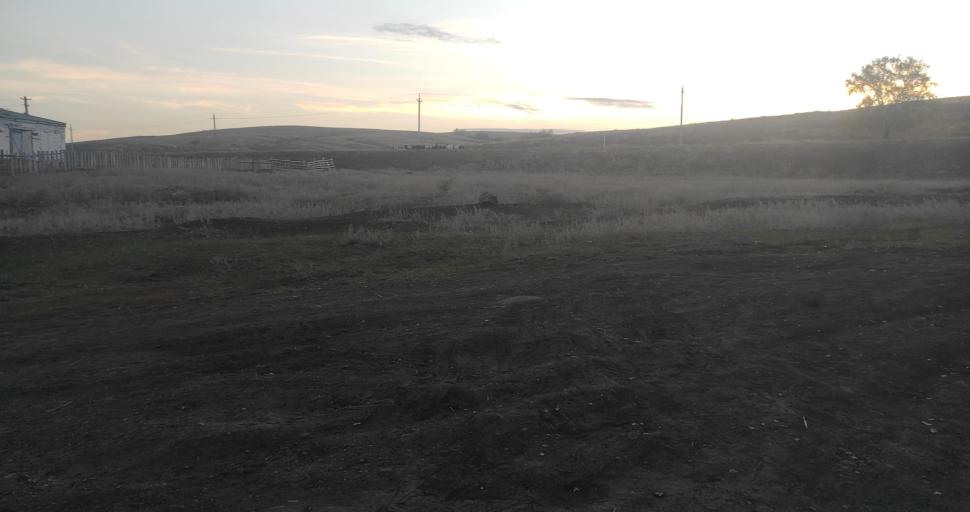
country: RU
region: Bashkortostan
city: Sibay
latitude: 52.6190
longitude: 58.5861
